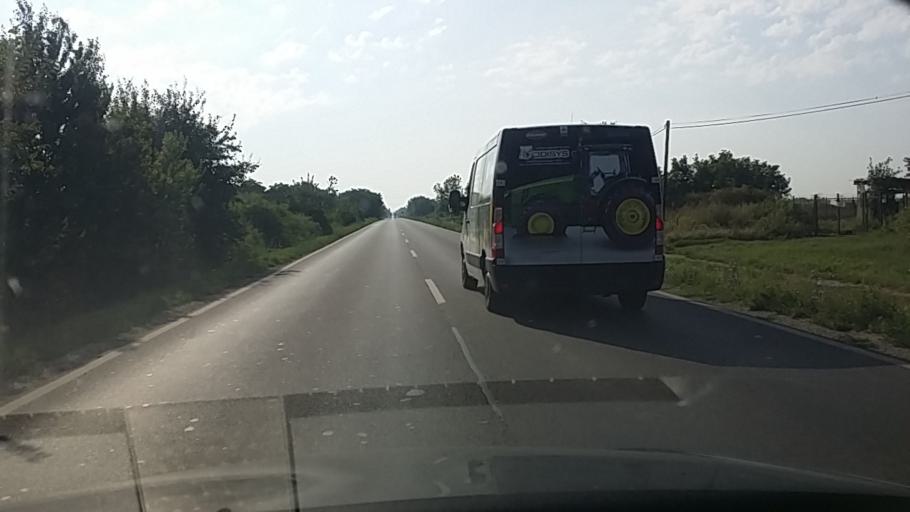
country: HU
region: Bekes
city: Kondoros
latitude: 46.8058
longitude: 20.7017
